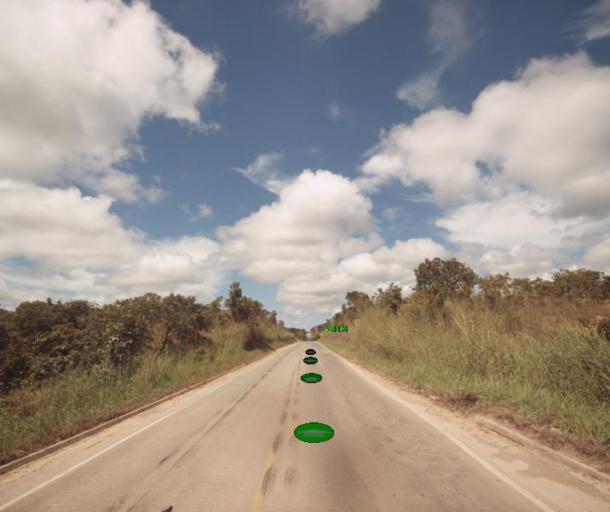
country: BR
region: Goias
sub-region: Padre Bernardo
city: Padre Bernardo
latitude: -15.2085
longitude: -48.2821
